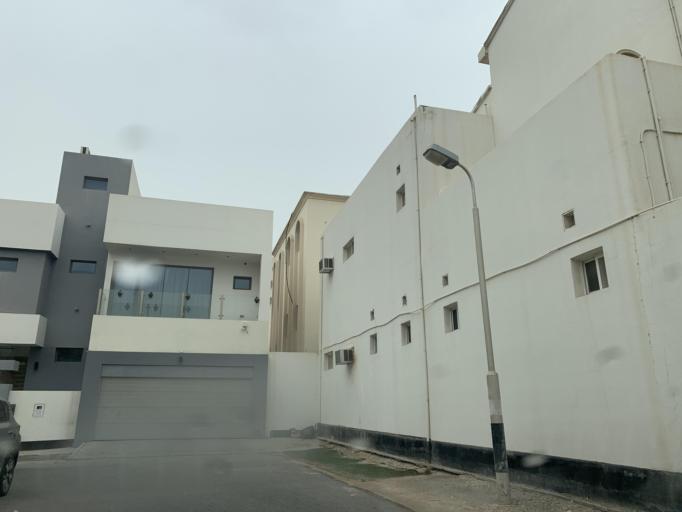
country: BH
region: Northern
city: Ar Rifa'
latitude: 26.1473
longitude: 50.5266
